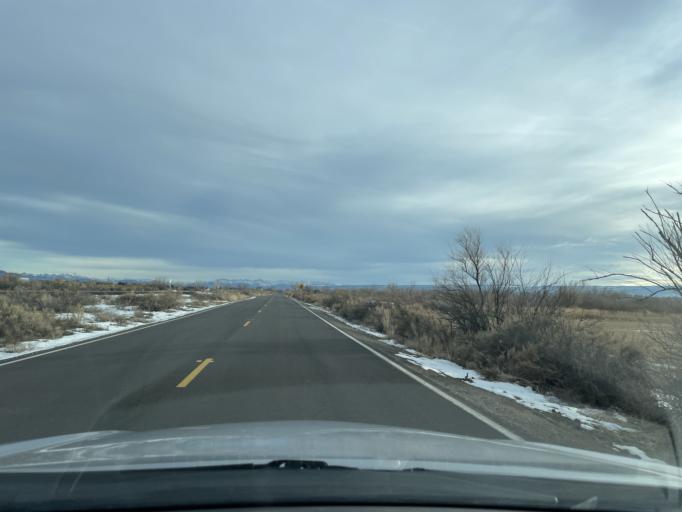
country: US
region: Colorado
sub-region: Montrose County
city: Olathe
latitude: 38.6510
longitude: -107.9958
